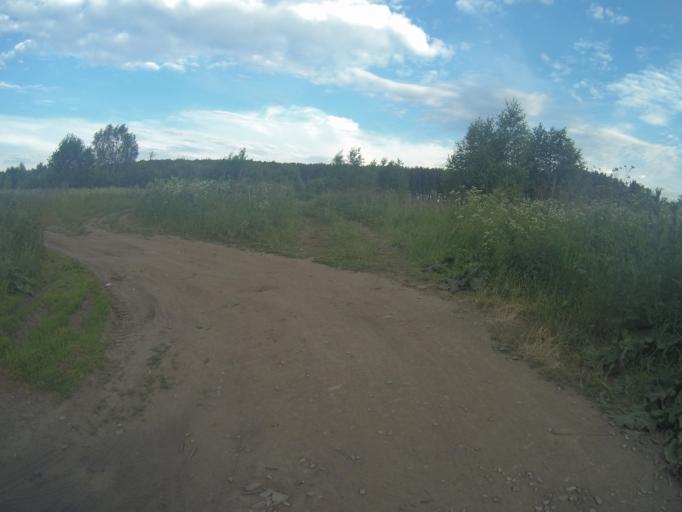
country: RU
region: Vladimir
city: Vladimir
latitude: 56.1940
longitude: 40.3786
